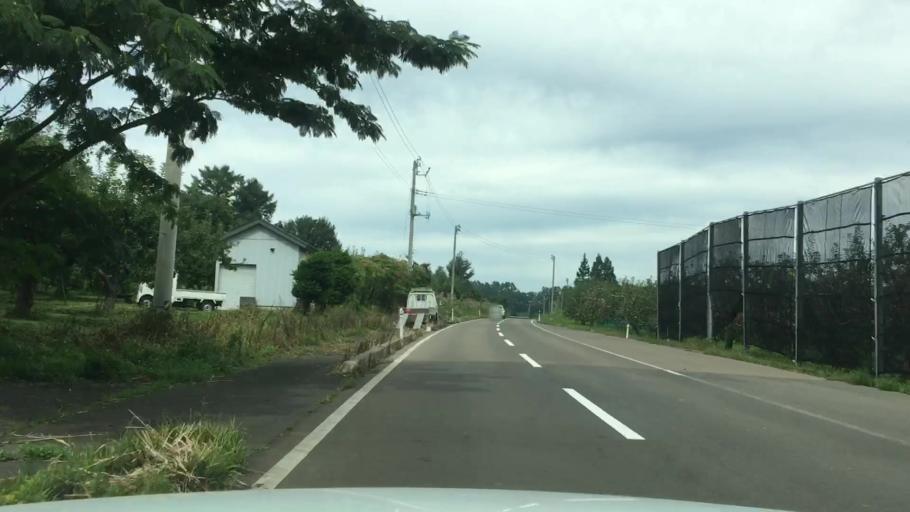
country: JP
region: Aomori
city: Hirosaki
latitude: 40.6720
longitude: 140.3860
